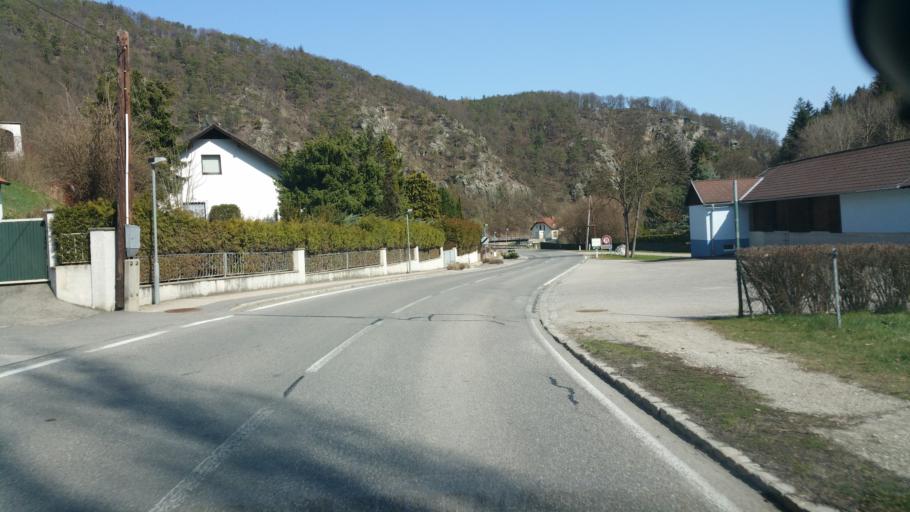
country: AT
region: Lower Austria
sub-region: Politischer Bezirk Krems
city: Senftenberg
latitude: 48.4552
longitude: 15.5368
